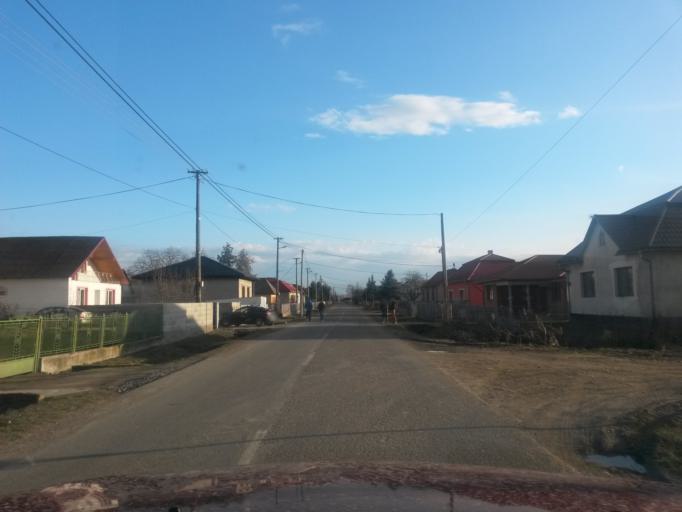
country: SK
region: Kosicky
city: Sobrance
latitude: 48.7072
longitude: 22.1050
